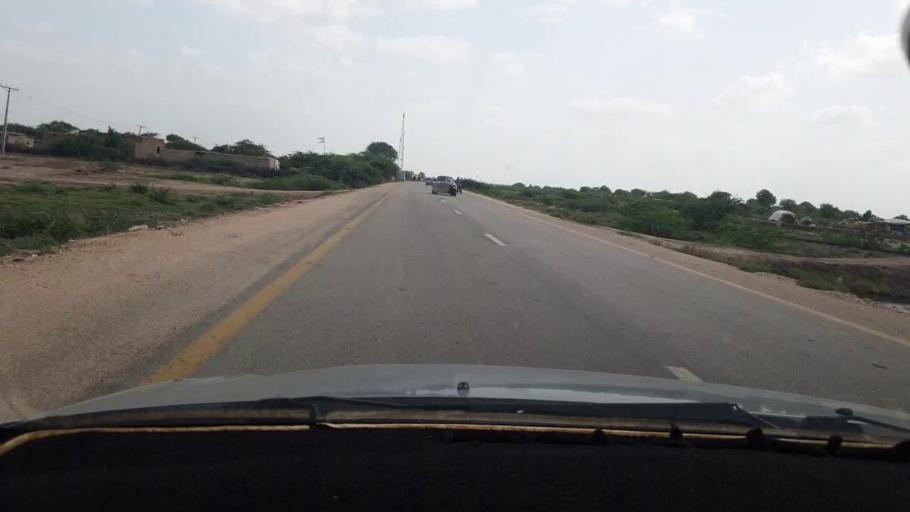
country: PK
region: Sindh
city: Naukot
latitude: 24.9963
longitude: 69.2903
